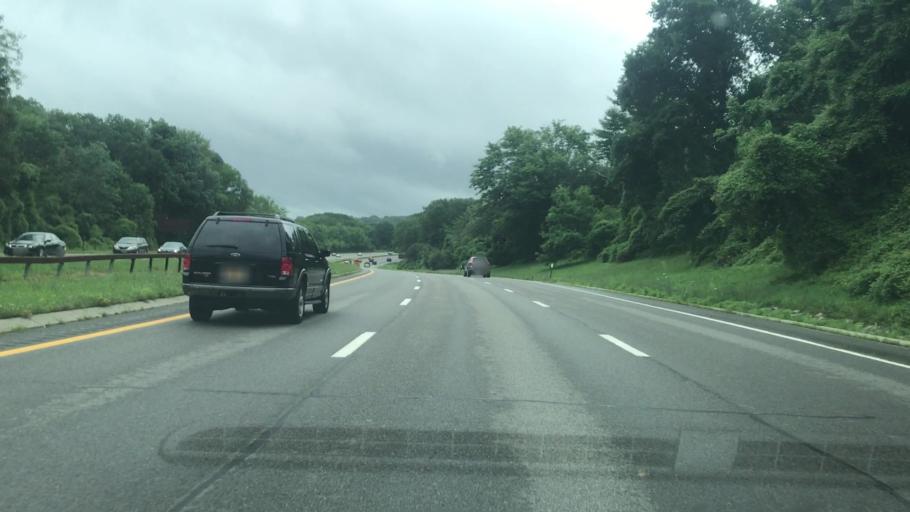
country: US
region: New York
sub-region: Westchester County
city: Yorktown Heights
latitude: 41.2761
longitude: -73.8160
